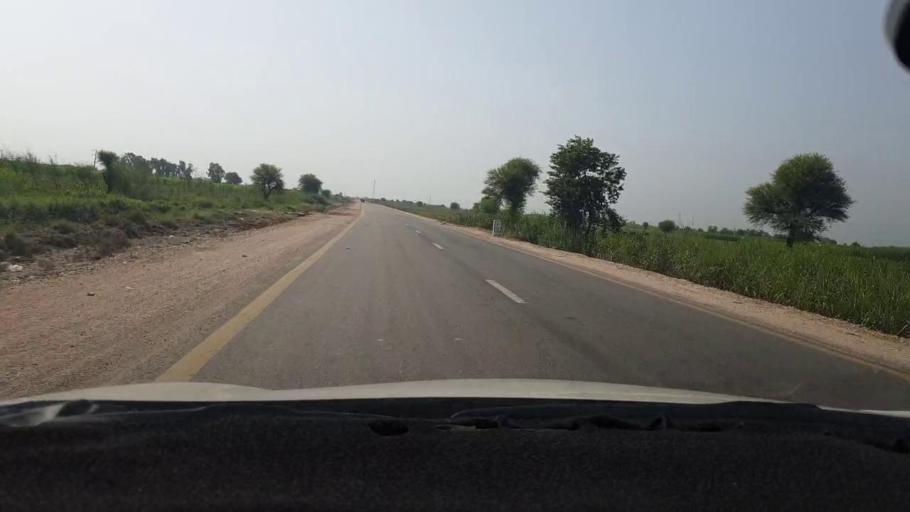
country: PK
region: Sindh
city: Jhol
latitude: 25.8431
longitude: 69.0617
